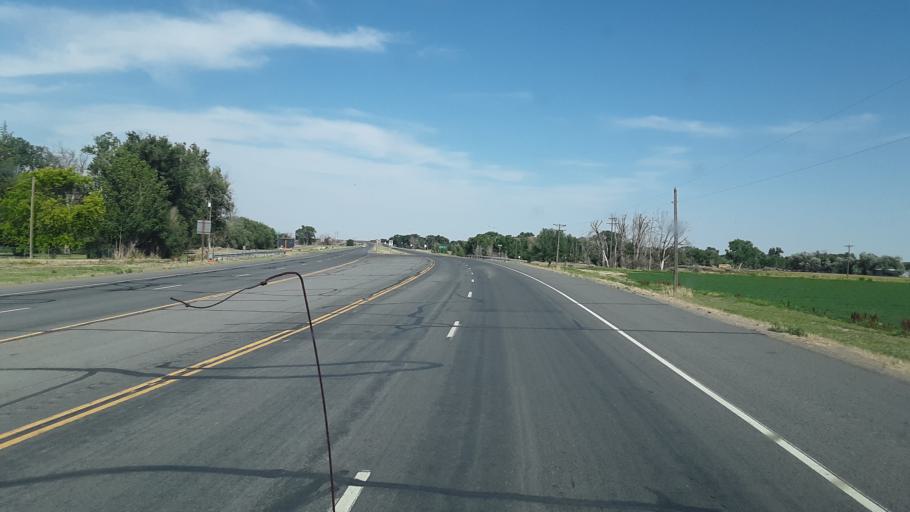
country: US
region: Colorado
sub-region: Otero County
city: Rocky Ford
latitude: 38.1048
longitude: -103.8586
